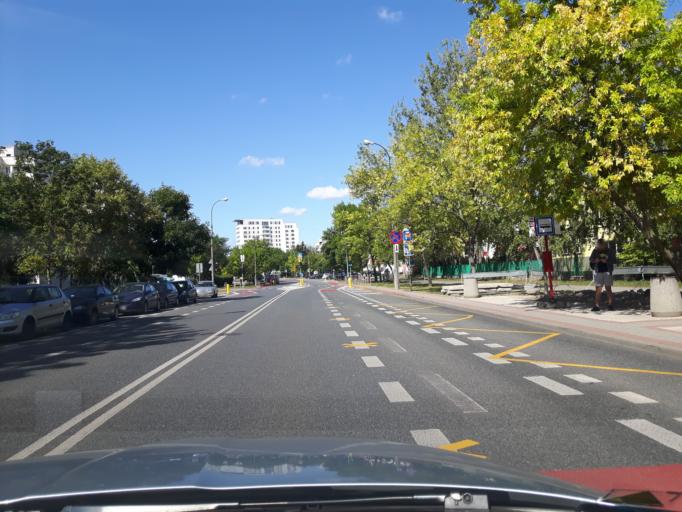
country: PL
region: Masovian Voivodeship
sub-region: Warszawa
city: Ursynow
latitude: 52.1486
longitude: 21.0411
